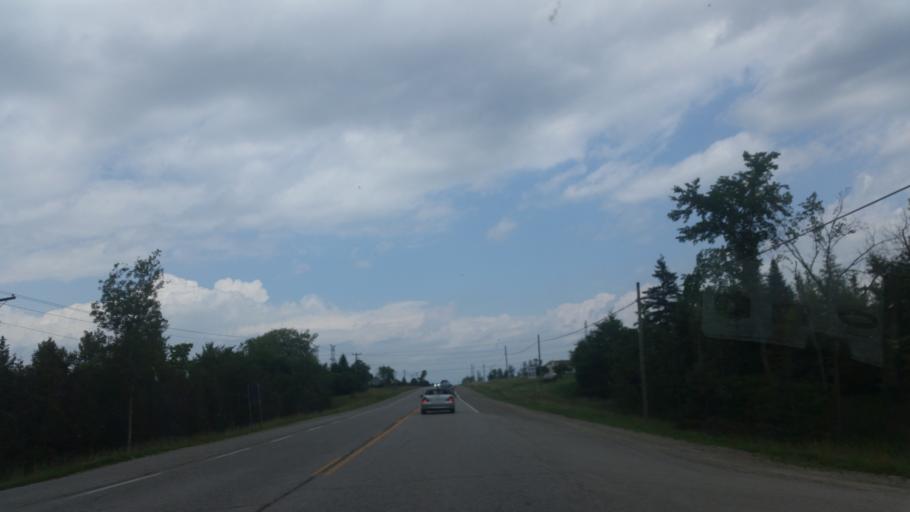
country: CA
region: Ontario
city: Orangeville
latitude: 43.7179
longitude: -80.1123
